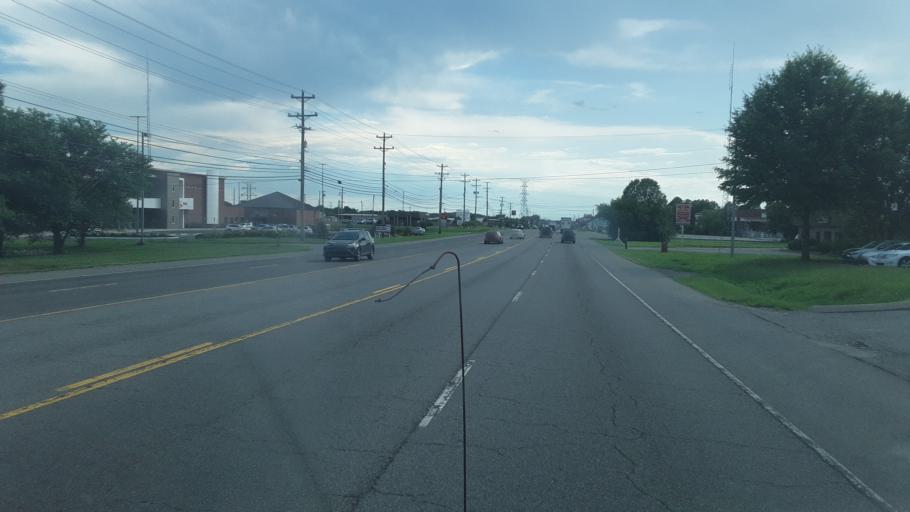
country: US
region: Tennessee
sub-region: Montgomery County
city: Clarksville
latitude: 36.5599
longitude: -87.3167
